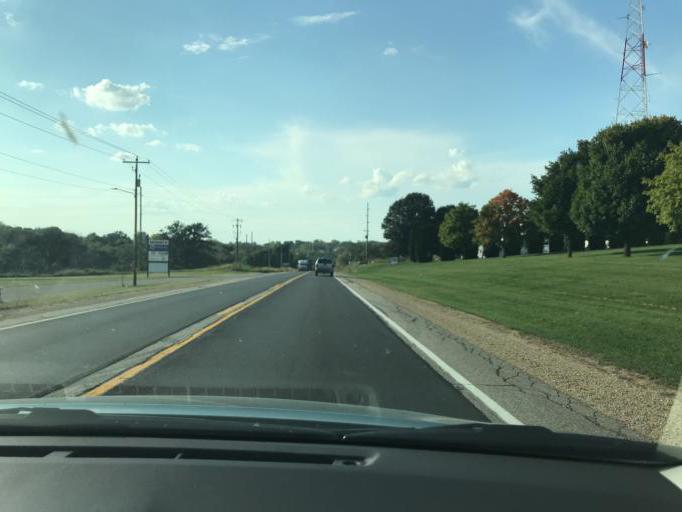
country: US
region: Wisconsin
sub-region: Grant County
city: Platteville
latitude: 42.7216
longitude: -90.4690
